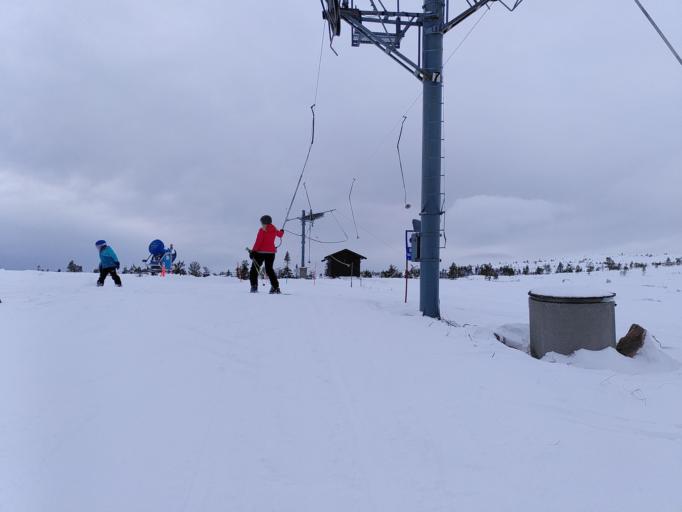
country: NO
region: Buskerud
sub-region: Flesberg
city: Lampeland
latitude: 59.7996
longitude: 9.3866
